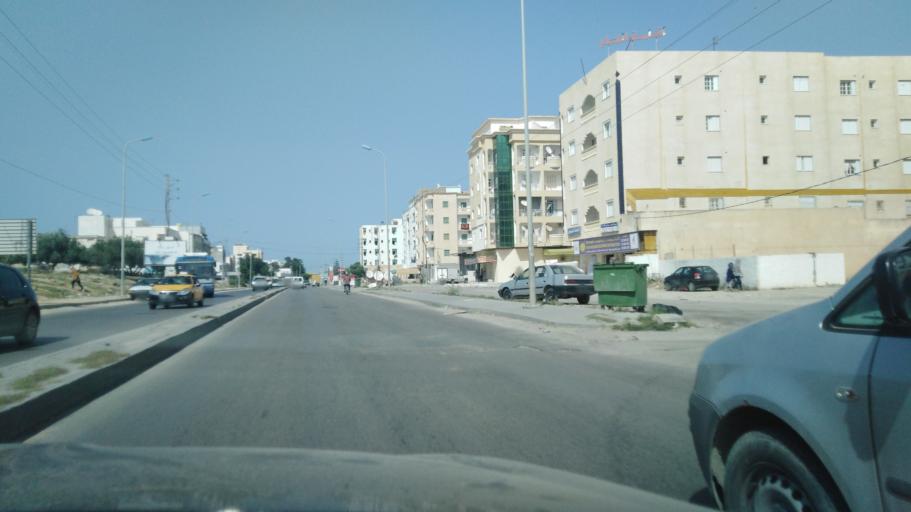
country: TN
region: Susah
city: Sousse
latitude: 35.8096
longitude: 10.6235
